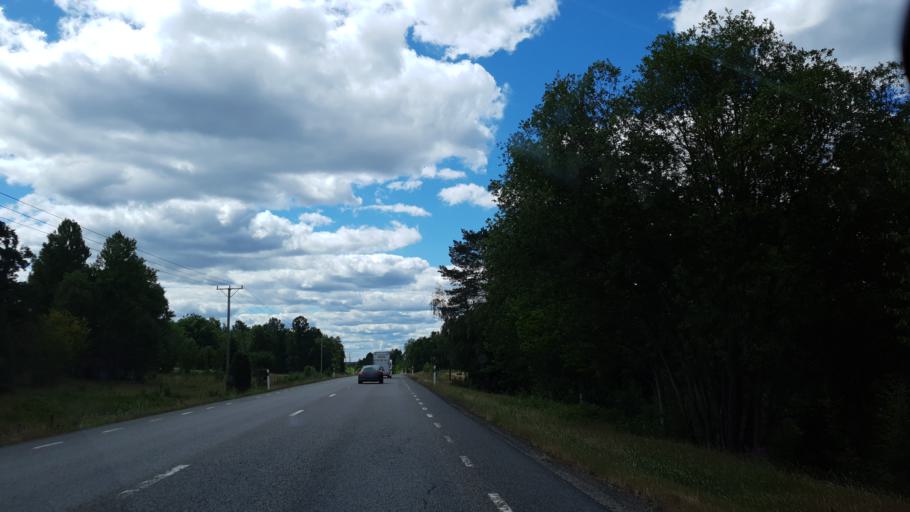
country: SE
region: Kronoberg
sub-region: Vaxjo Kommun
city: Braas
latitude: 57.1611
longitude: 15.1614
